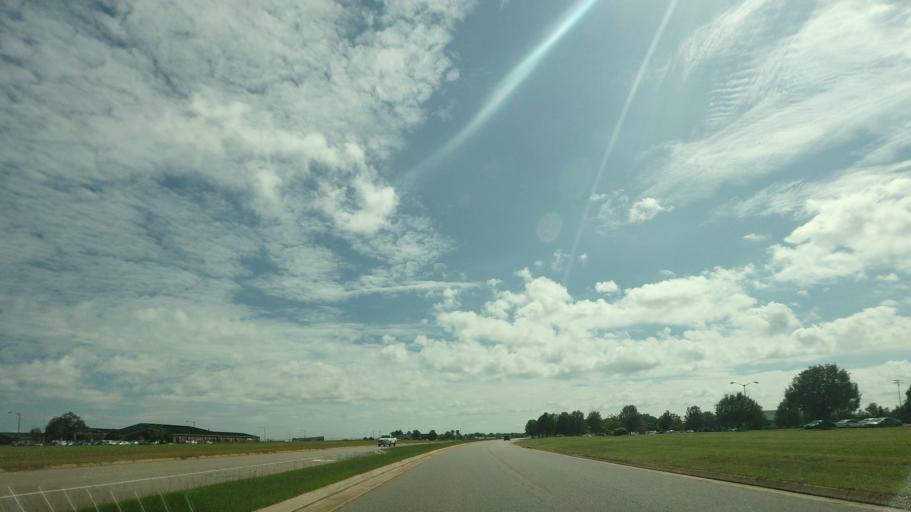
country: US
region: Georgia
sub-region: Houston County
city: Centerville
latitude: 32.5465
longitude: -83.6766
